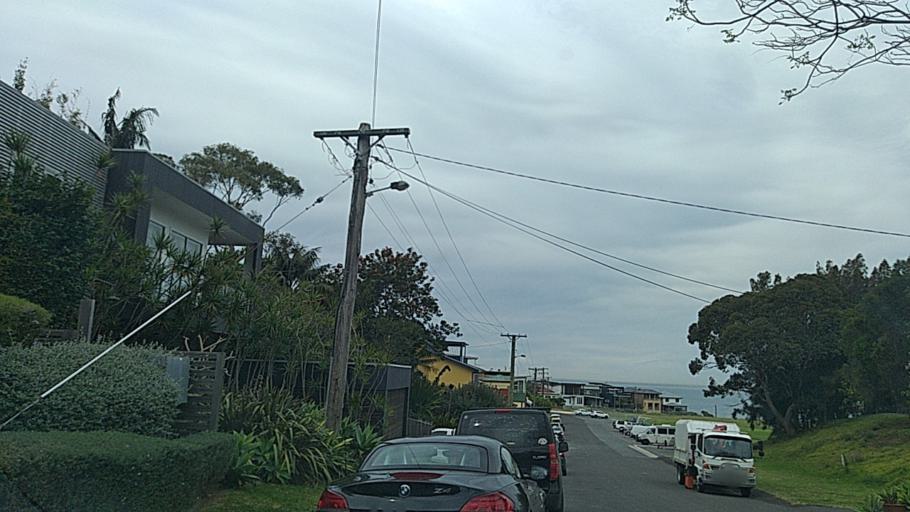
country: AU
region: New South Wales
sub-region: Wollongong
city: Bulli
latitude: -34.2917
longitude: 150.9423
